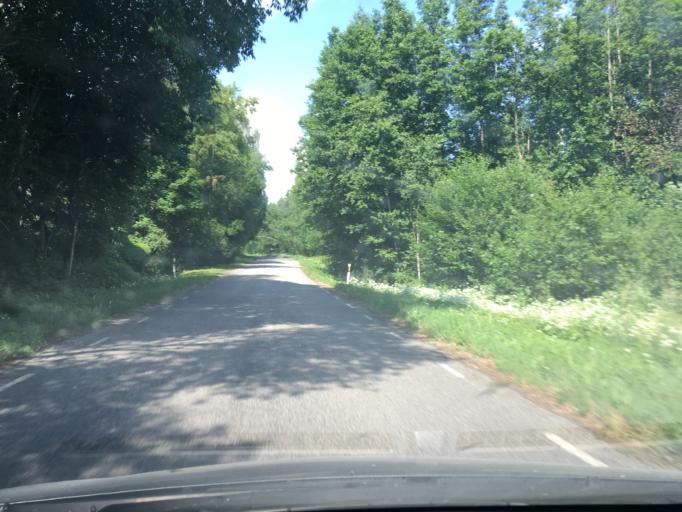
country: EE
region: Raplamaa
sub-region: Maerjamaa vald
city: Marjamaa
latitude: 58.7445
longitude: 24.4111
